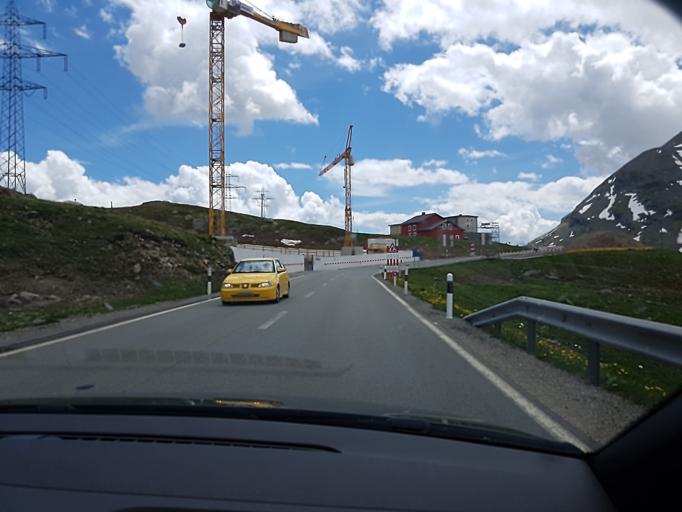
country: CH
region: Grisons
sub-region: Bernina District
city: Poschiavo
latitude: 46.4133
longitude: 10.0210
